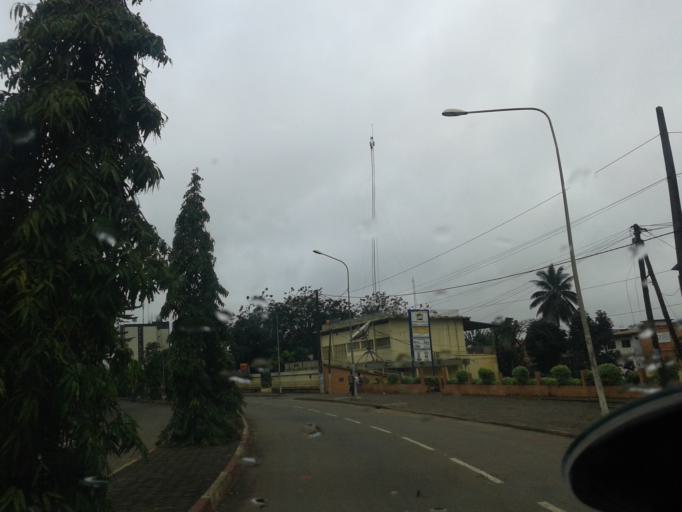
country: CM
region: Centre
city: Yaounde
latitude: 3.8739
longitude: 11.5176
